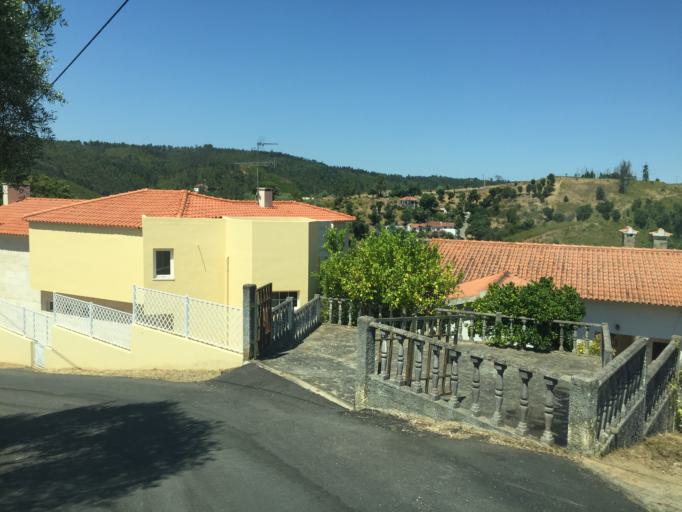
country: PT
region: Santarem
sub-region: Constancia
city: Constancia
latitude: 39.5684
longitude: -8.2985
